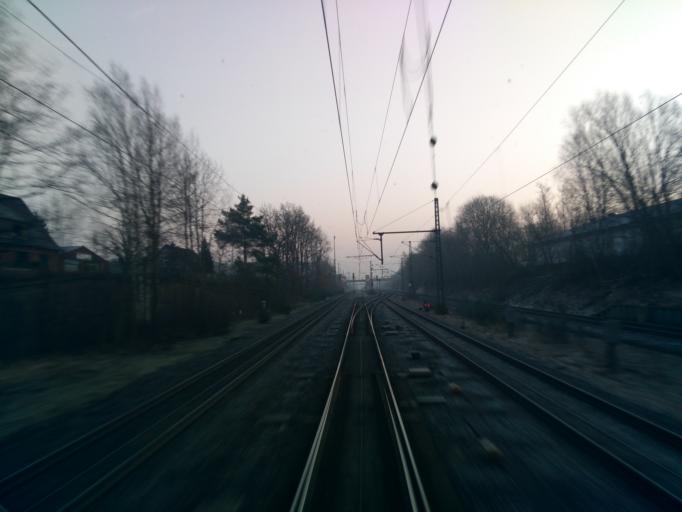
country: DE
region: Lower Saxony
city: Tostedt
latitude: 53.2697
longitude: 9.7271
